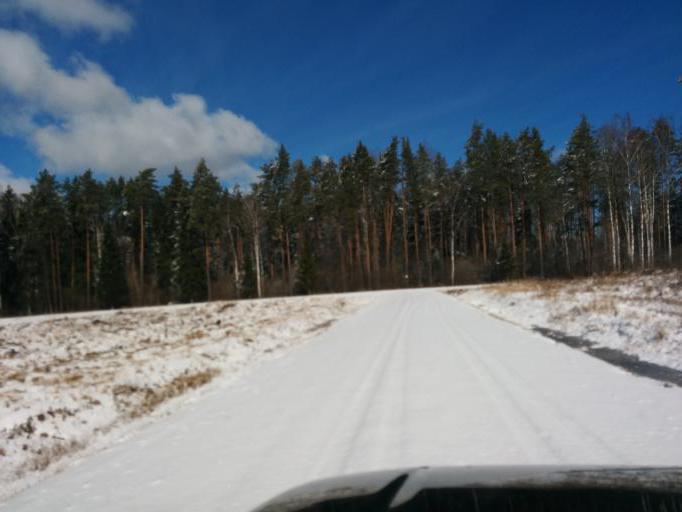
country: LV
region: Jelgava
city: Jelgava
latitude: 56.6203
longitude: 23.6455
